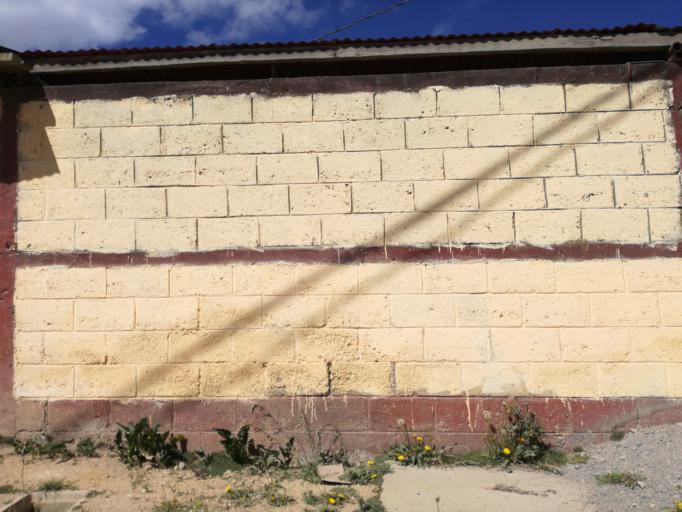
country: GT
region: Quetzaltenango
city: Almolonga
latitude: 14.7886
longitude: -91.5390
